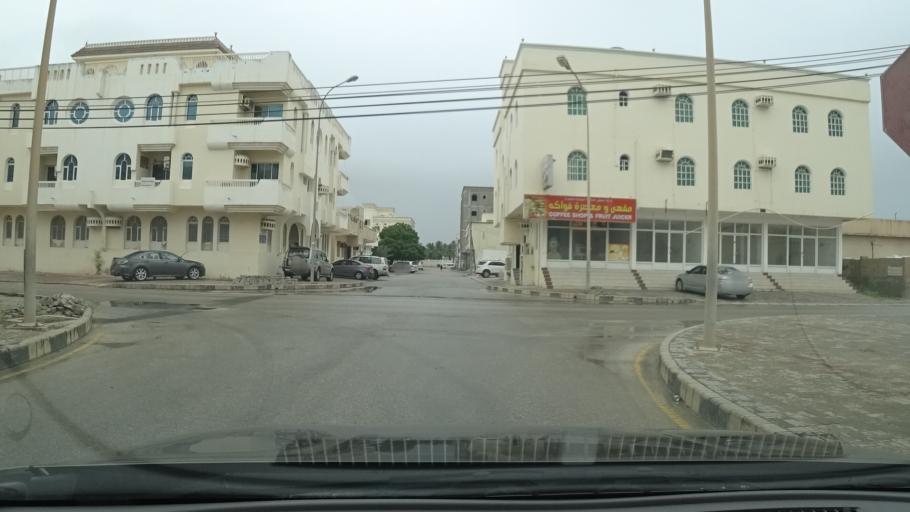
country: OM
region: Zufar
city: Salalah
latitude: 17.0247
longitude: 54.1587
